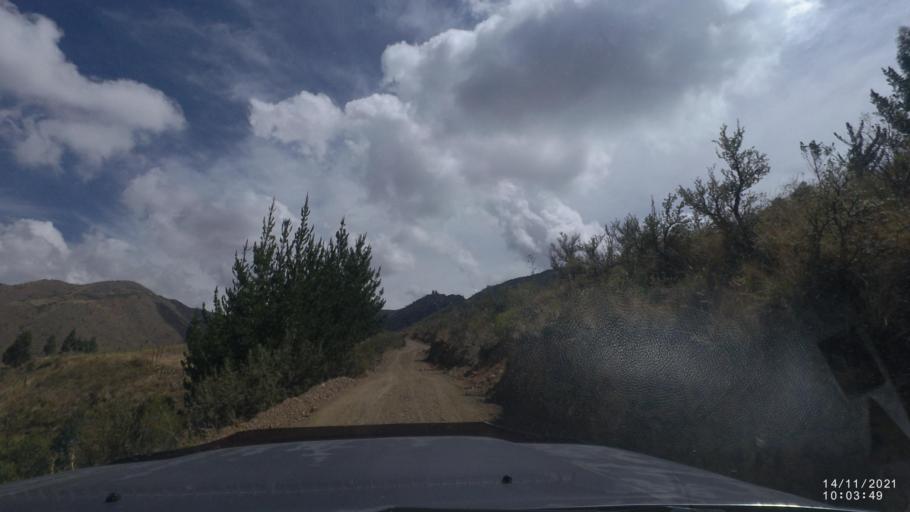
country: BO
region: Cochabamba
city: Cochabamba
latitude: -17.3500
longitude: -66.0920
